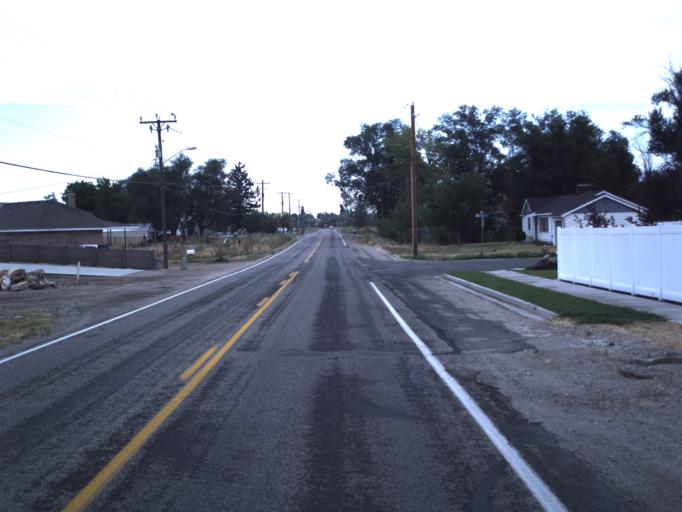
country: US
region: Utah
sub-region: Weber County
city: Hooper
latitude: 41.1351
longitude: -112.1125
